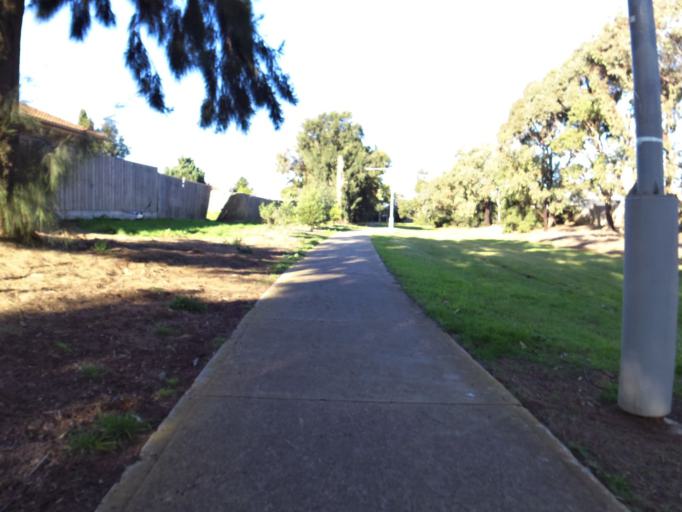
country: AU
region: Victoria
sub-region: Wyndham
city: Hoppers Crossing
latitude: -37.8651
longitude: 144.6926
